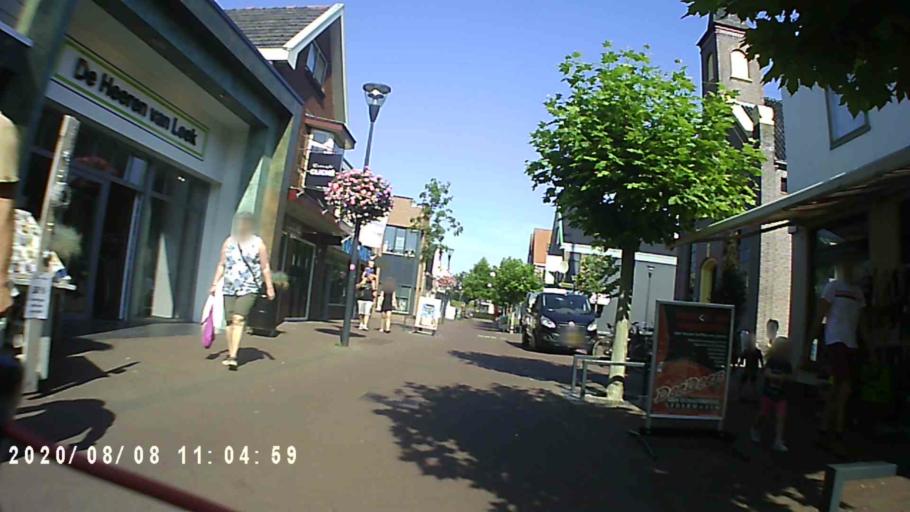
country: NL
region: Groningen
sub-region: Gemeente Leek
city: Leek
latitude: 53.1628
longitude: 6.3918
